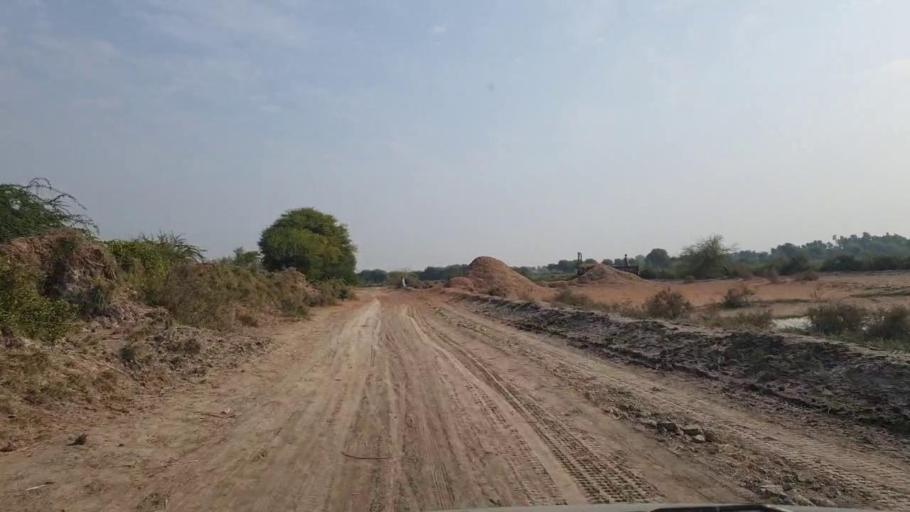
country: PK
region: Sindh
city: Talhar
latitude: 24.9039
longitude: 68.8964
